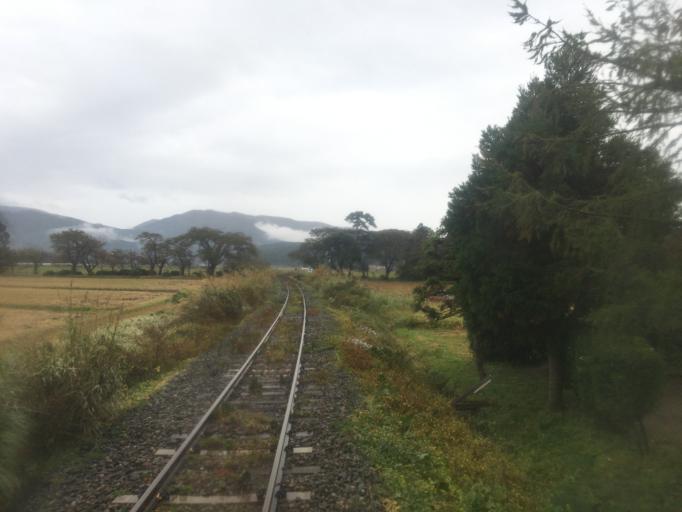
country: JP
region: Yamagata
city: Tsuruoka
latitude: 38.7914
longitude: 139.9823
